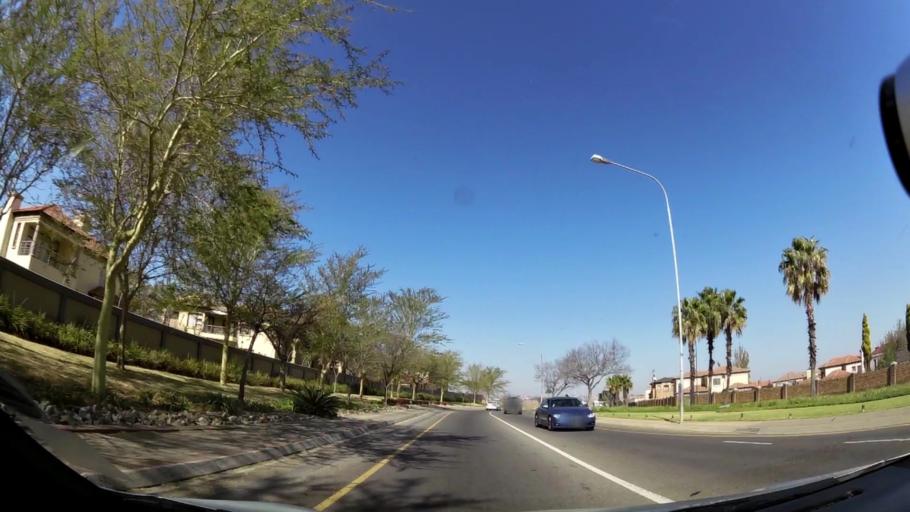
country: ZA
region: Gauteng
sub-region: City of Johannesburg Metropolitan Municipality
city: Midrand
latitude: -25.9363
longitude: 28.1314
